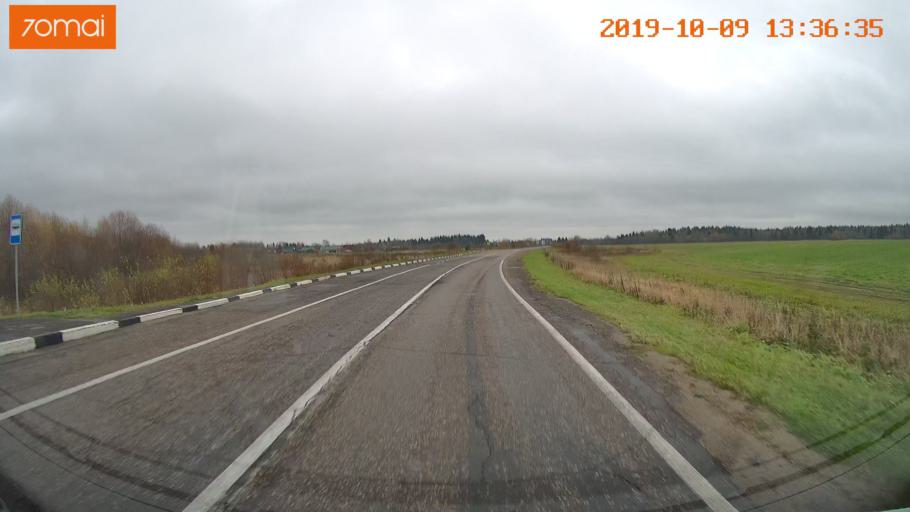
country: RU
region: Jaroslavl
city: Lyubim
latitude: 58.3402
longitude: 41.1003
